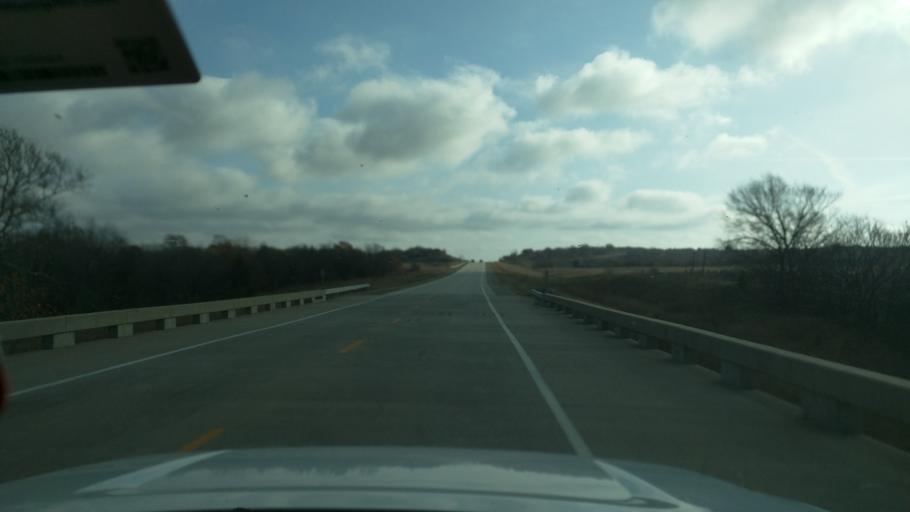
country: US
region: Kansas
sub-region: Chautauqua County
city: Sedan
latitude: 37.0826
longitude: -96.1241
